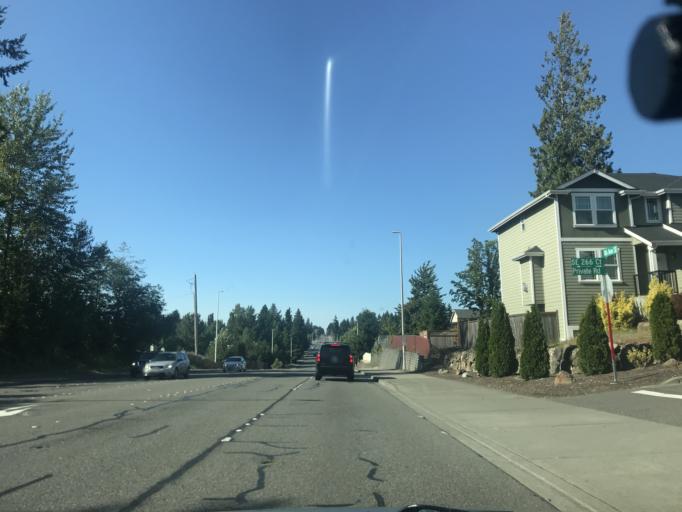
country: US
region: Washington
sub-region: King County
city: Lea Hill
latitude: 47.3627
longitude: -122.1867
